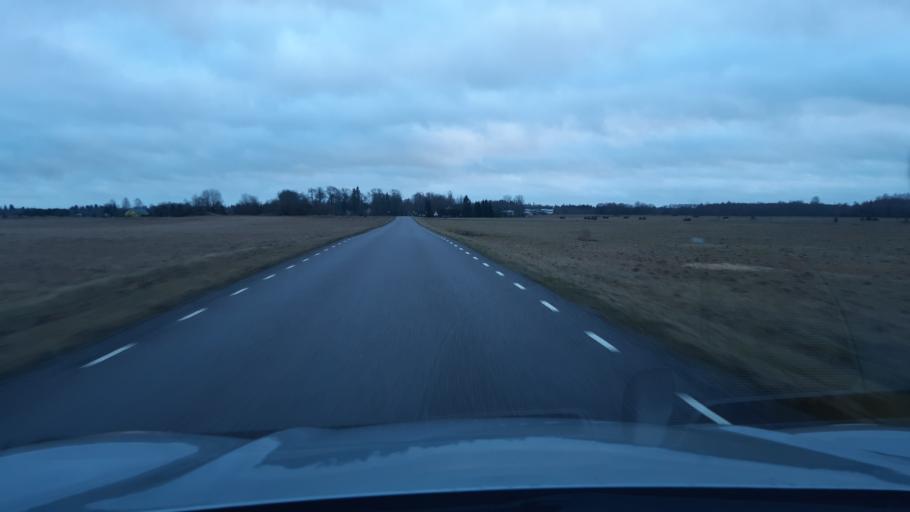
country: EE
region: Raplamaa
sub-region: Kohila vald
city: Kohila
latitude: 59.1208
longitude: 24.6777
